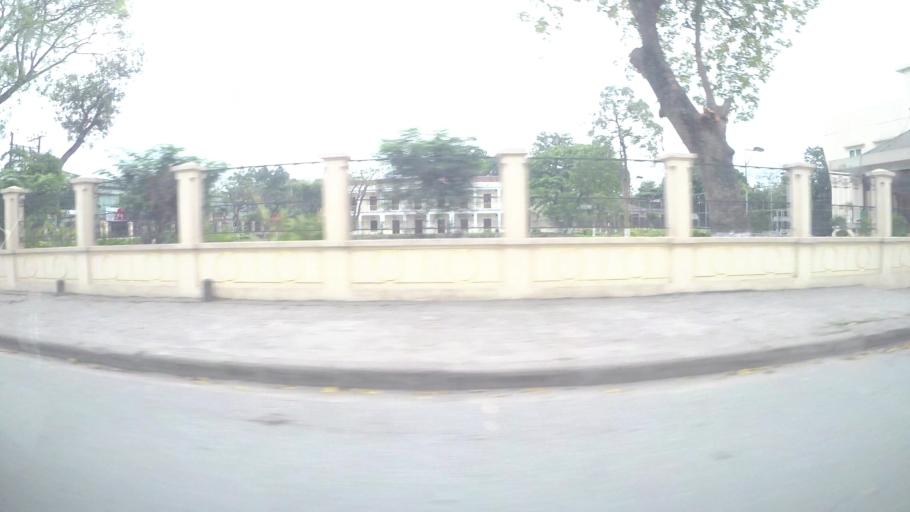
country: VN
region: Ha Noi
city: Hoan Kiem
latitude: 21.0652
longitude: 105.8934
